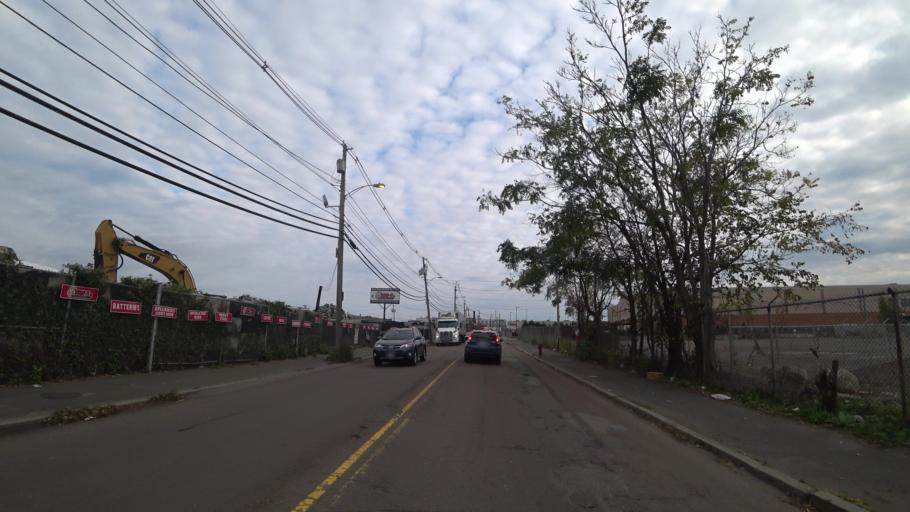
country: US
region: Massachusetts
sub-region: Middlesex County
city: Everett
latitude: 42.4014
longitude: -71.0515
